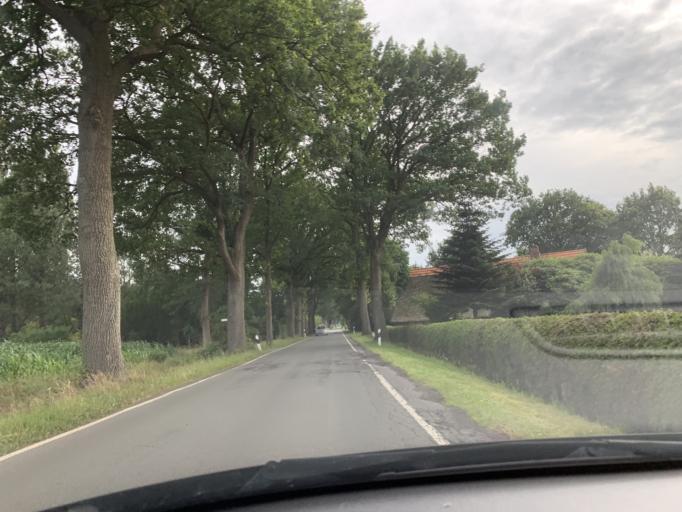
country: DE
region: Lower Saxony
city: Westerstede
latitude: 53.2831
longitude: 7.9200
